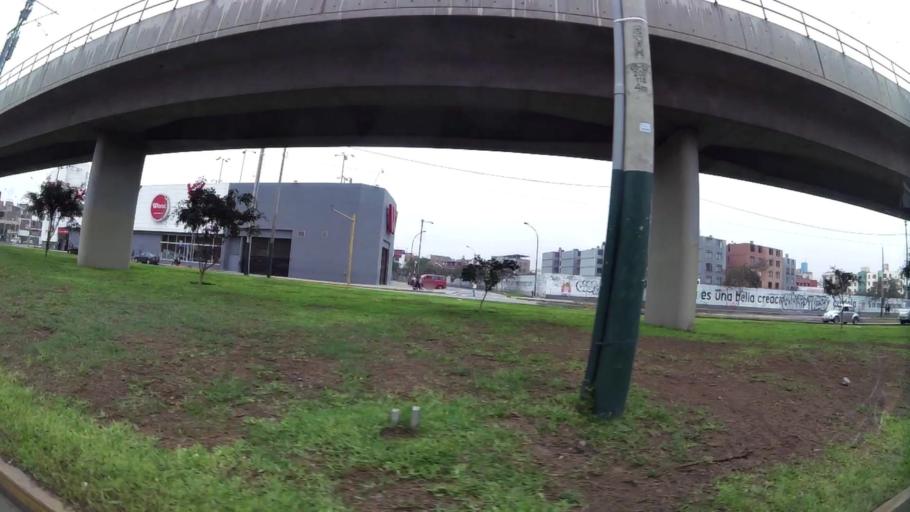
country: PE
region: Lima
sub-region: Lima
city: Surco
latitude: -12.1436
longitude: -76.9903
